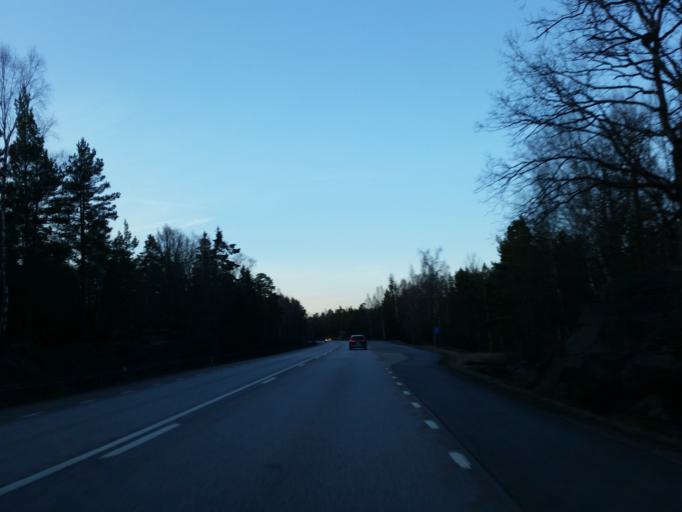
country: SE
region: Kalmar
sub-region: Oskarshamns Kommun
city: Oskarshamn
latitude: 57.5082
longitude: 16.5021
